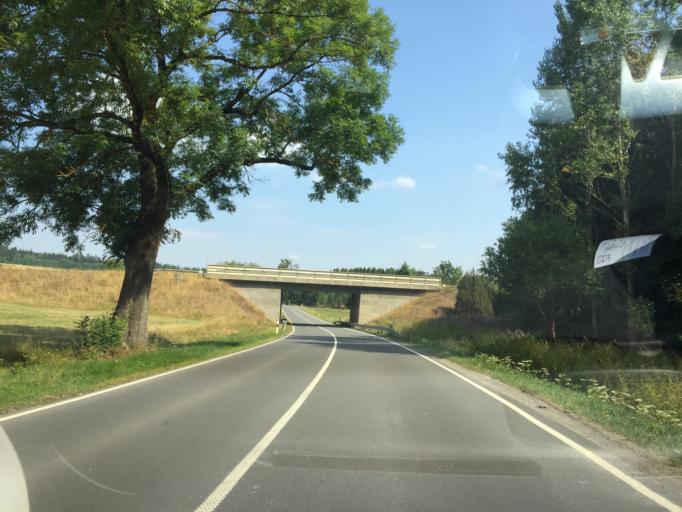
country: DE
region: Saxony-Anhalt
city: Elbingerode
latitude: 51.7597
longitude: 10.7839
